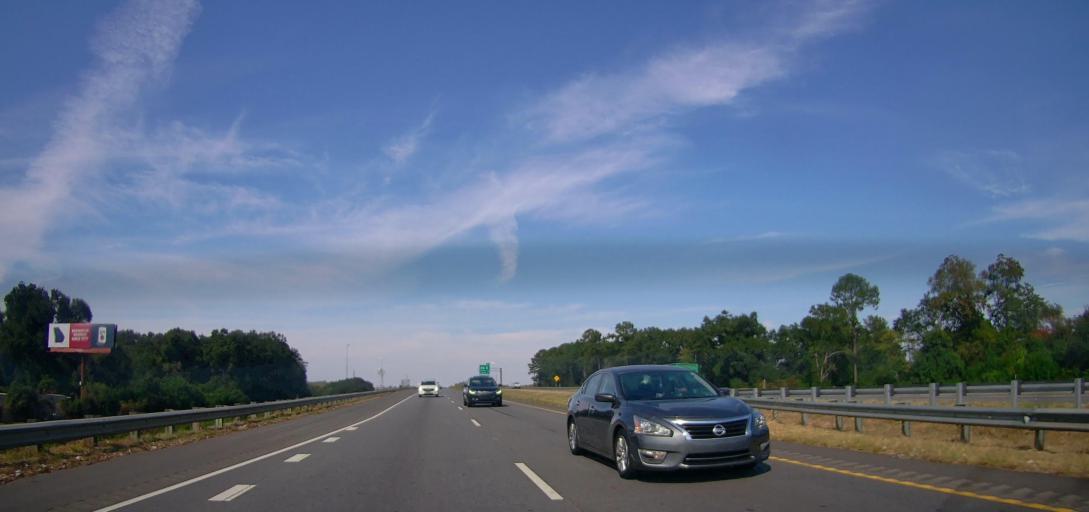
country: US
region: Georgia
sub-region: Dougherty County
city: Albany
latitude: 31.5765
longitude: -84.1116
